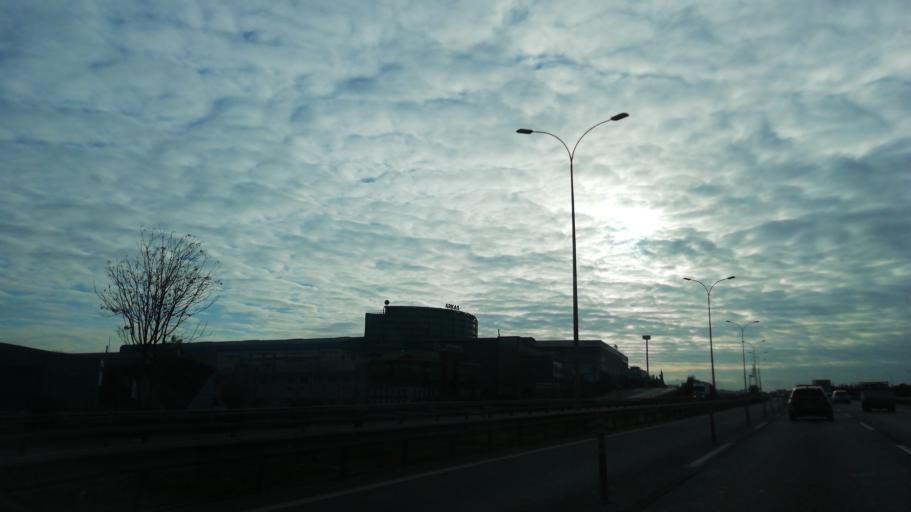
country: TR
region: Kocaeli
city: Balcik
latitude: 40.8862
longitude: 29.3753
